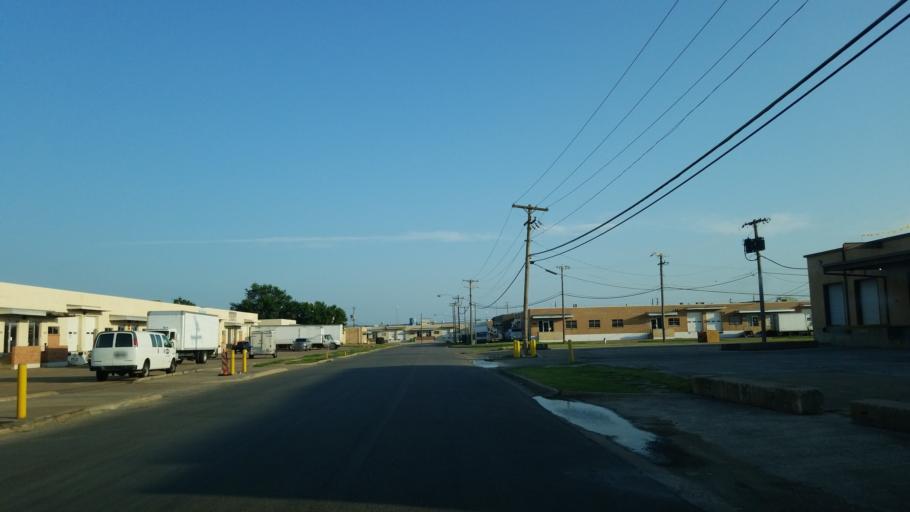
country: US
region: Texas
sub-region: Dallas County
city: Farmers Branch
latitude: 32.8758
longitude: -96.8781
